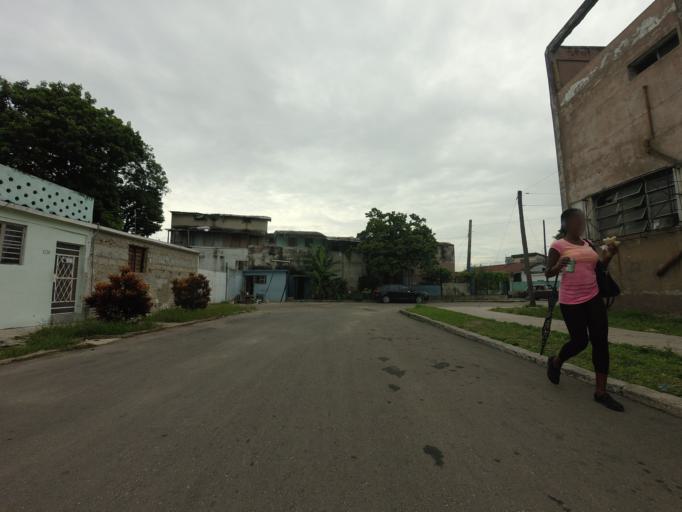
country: CU
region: La Habana
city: Havana
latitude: 23.1238
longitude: -82.3788
